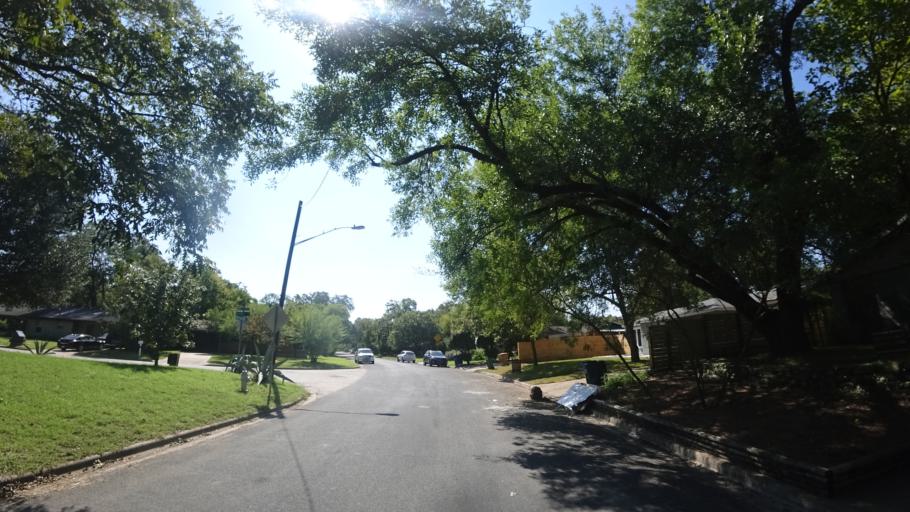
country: US
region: Texas
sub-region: Travis County
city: Austin
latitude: 30.3167
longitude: -97.6863
